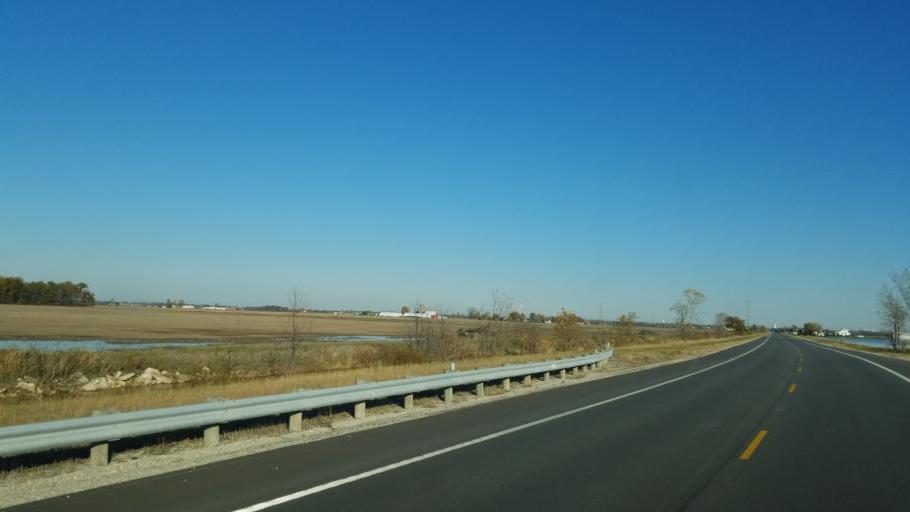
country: US
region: Ohio
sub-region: Ottawa County
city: Genoa
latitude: 41.5149
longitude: -83.4117
